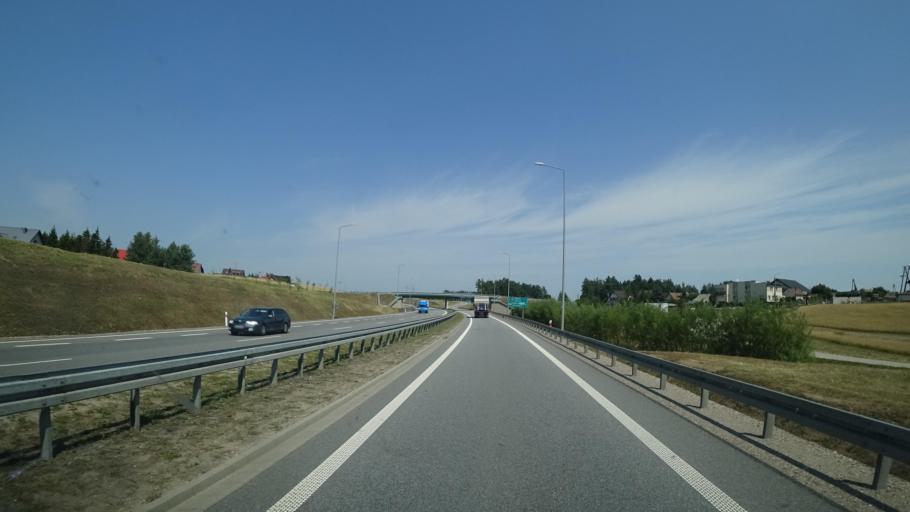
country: PL
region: Pomeranian Voivodeship
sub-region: Powiat koscierski
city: Koscierzyna
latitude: 54.1183
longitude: 18.0159
